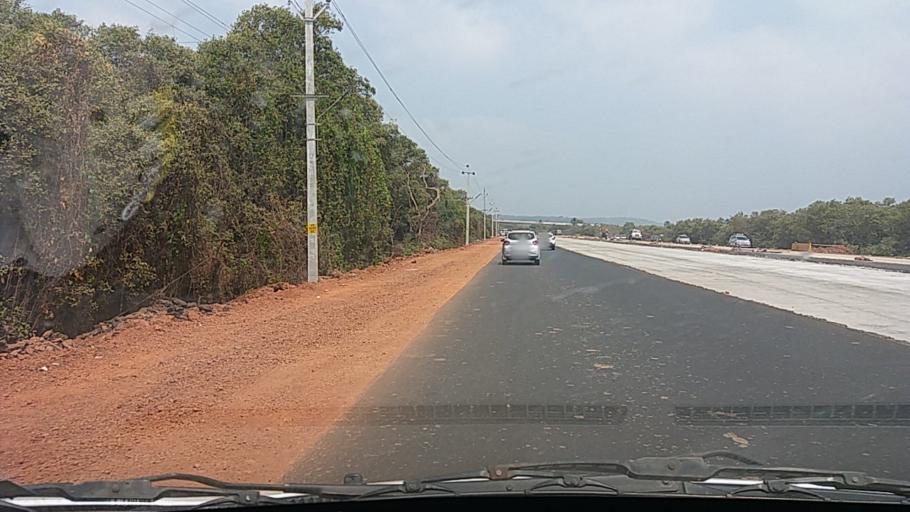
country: IN
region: Goa
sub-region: North Goa
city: Taleigao
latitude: 15.4864
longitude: 73.8462
